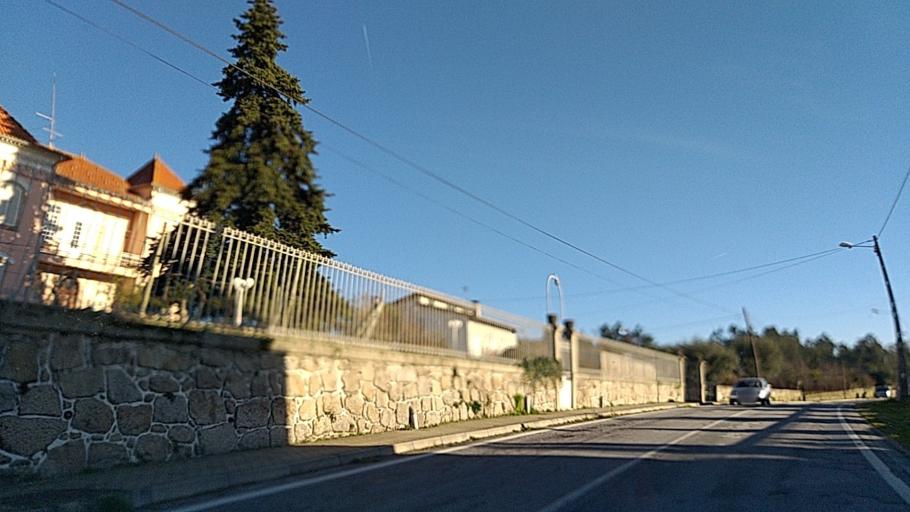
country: PT
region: Guarda
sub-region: Seia
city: Seia
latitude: 40.4686
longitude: -7.6819
